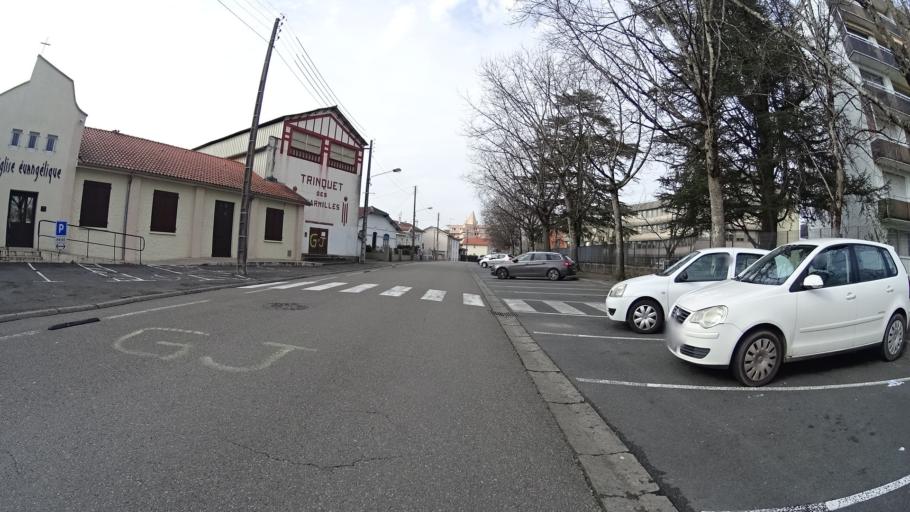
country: FR
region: Aquitaine
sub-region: Departement des Landes
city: Dax
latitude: 43.7004
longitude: -1.0556
